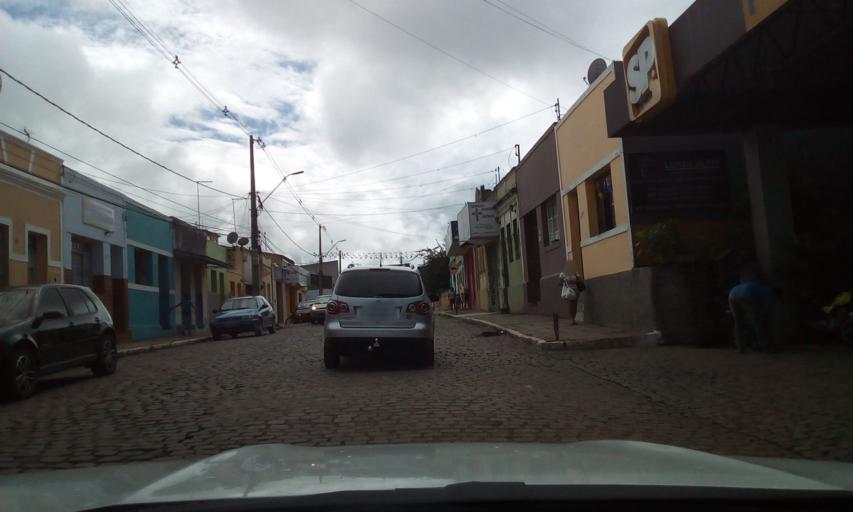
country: BR
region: Paraiba
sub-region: Areia
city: Areia
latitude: -6.9700
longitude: -35.6986
